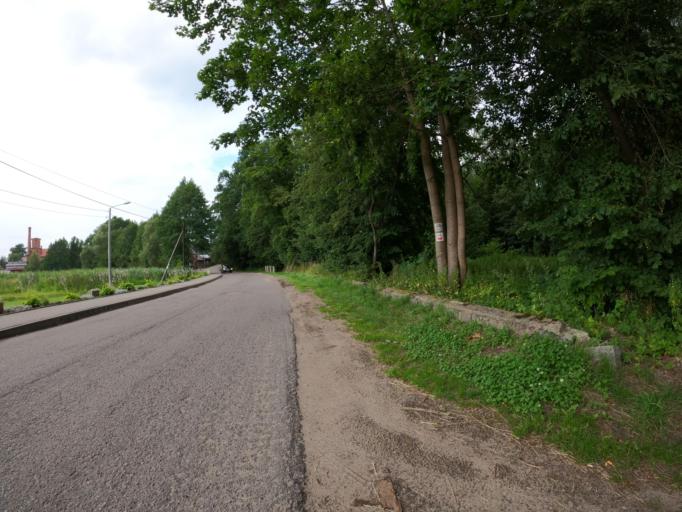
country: PL
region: West Pomeranian Voivodeship
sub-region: Powiat szczecinecki
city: Borne Sulinowo
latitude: 53.6751
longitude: 16.4921
